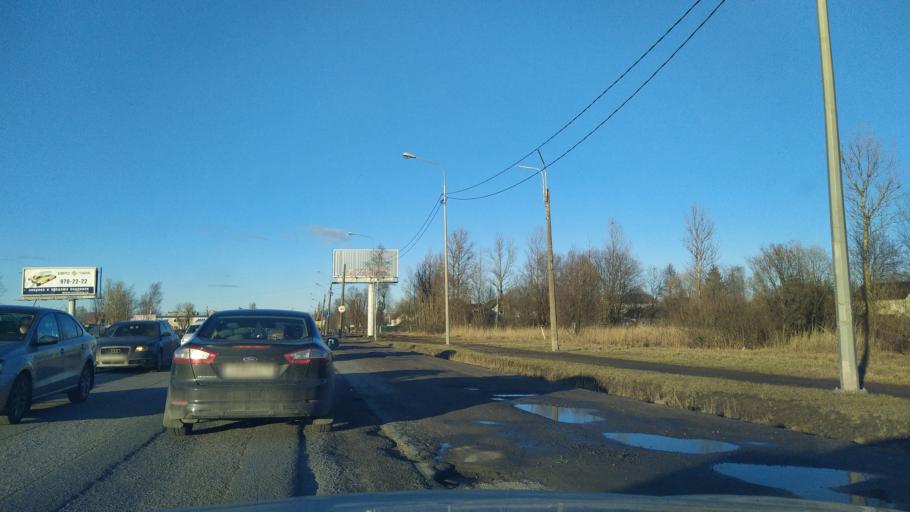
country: RU
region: St.-Petersburg
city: Uritsk
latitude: 59.8113
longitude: 30.1703
